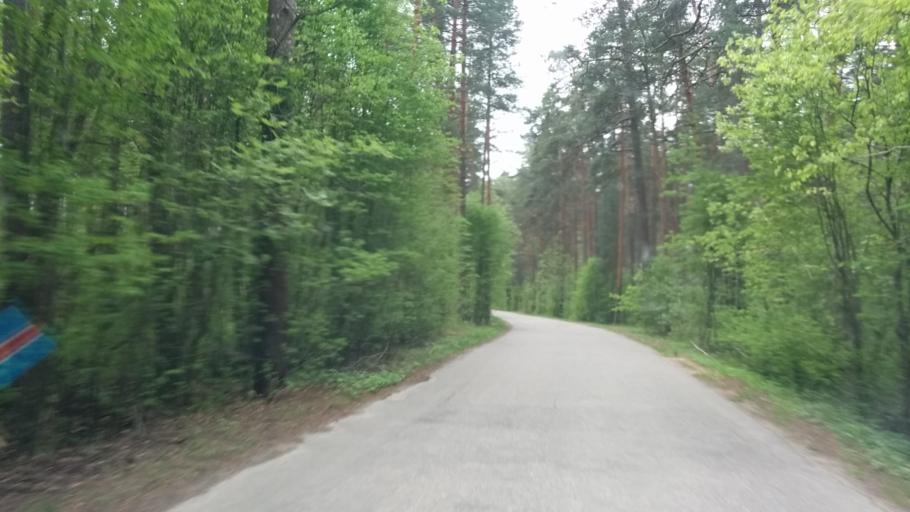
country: LV
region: Babite
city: Pinki
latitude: 56.9366
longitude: 23.9334
